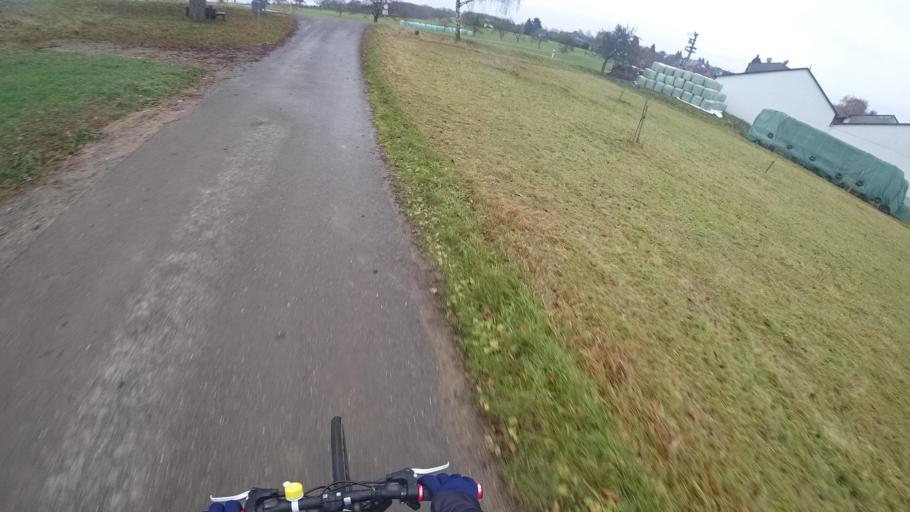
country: DE
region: Rheinland-Pfalz
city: Kratzenburg
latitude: 50.1785
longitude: 7.5463
